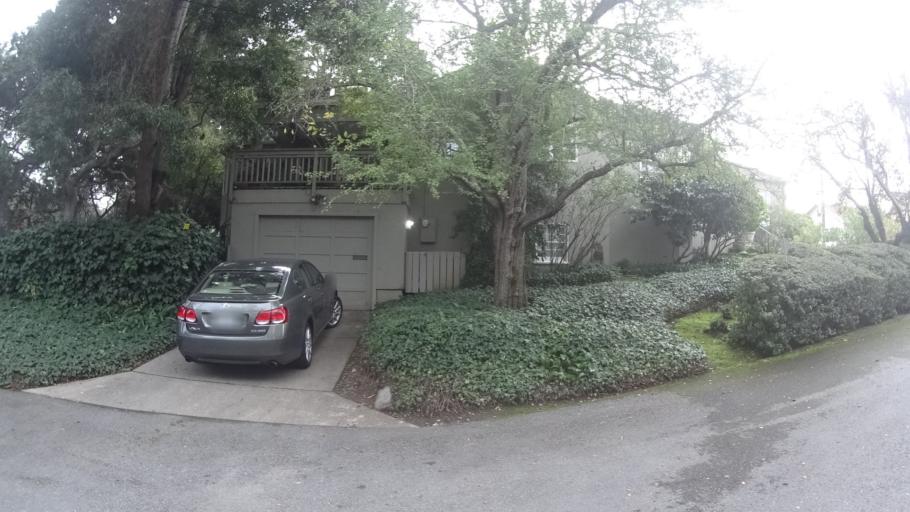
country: US
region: California
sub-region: San Mateo County
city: Burlingame
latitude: 37.5788
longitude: -122.3674
